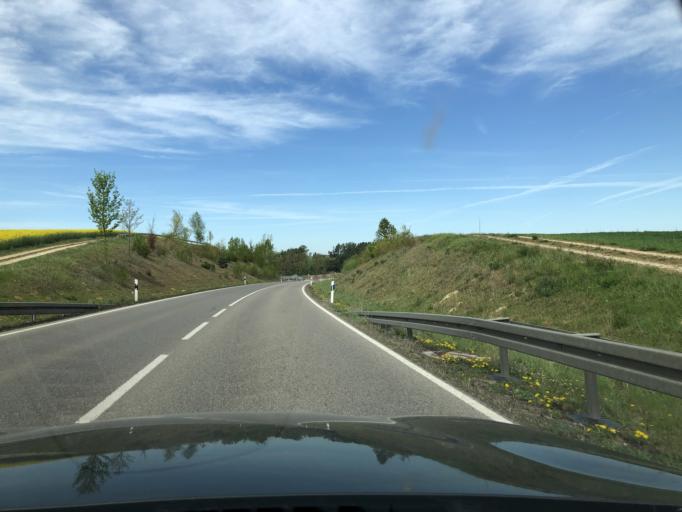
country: DE
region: Bavaria
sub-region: Swabia
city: Laugna
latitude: 48.5491
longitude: 10.7095
